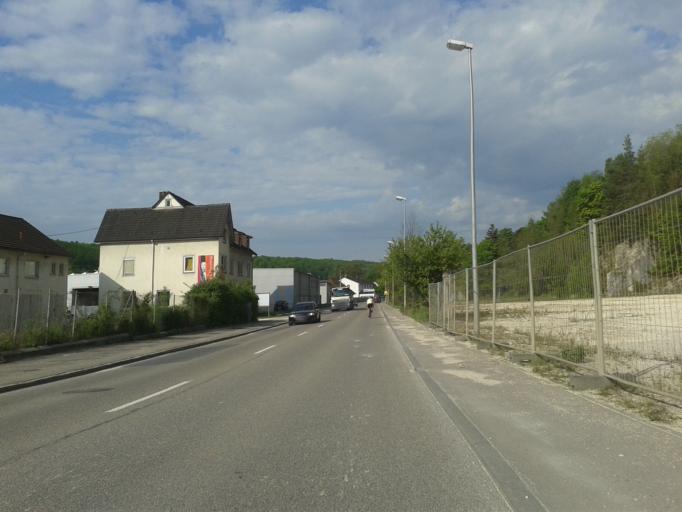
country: DE
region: Baden-Wuerttemberg
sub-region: Tuebingen Region
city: Dornstadt
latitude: 48.4203
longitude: 9.9023
